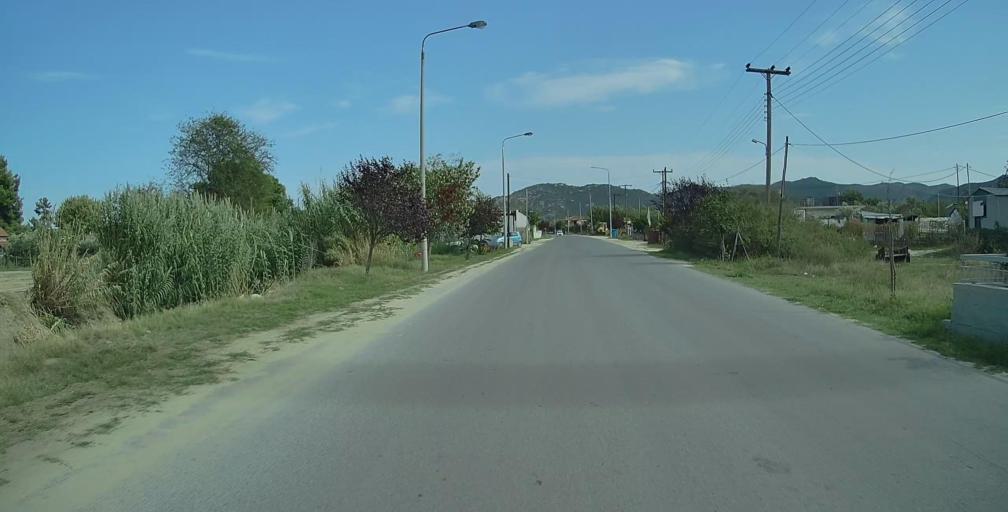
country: GR
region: Central Macedonia
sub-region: Nomos Chalkidikis
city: Sykia
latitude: 40.0381
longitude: 23.9490
